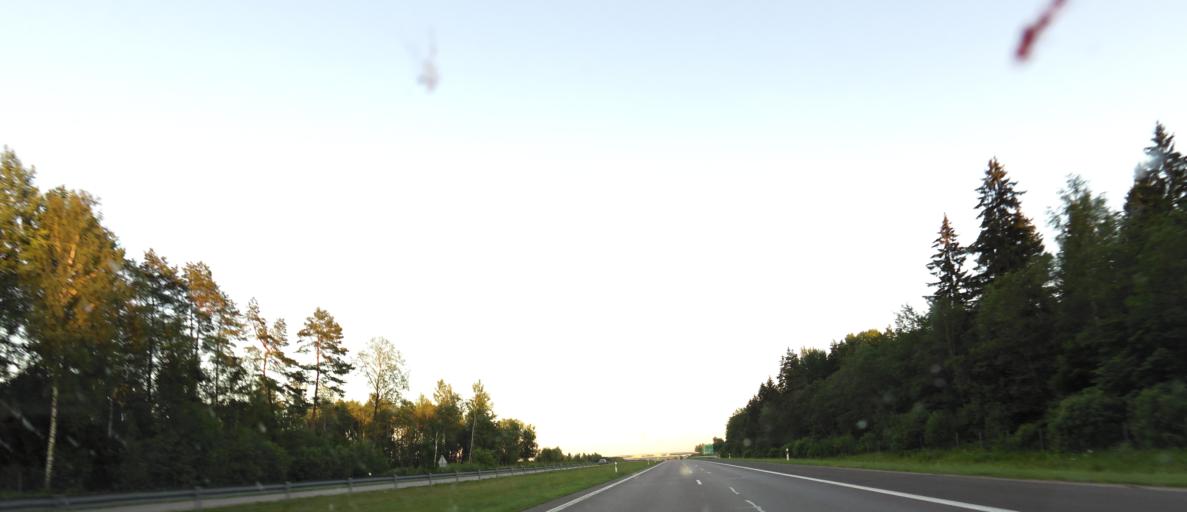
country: LT
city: Sirvintos
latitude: 54.9526
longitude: 24.9617
